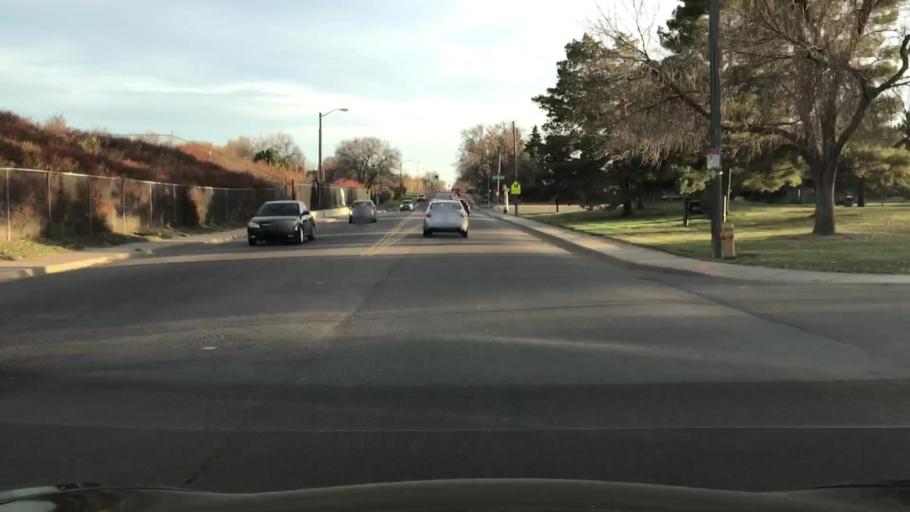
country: US
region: Colorado
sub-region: Arapahoe County
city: Glendale
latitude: 39.7343
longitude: -104.9035
